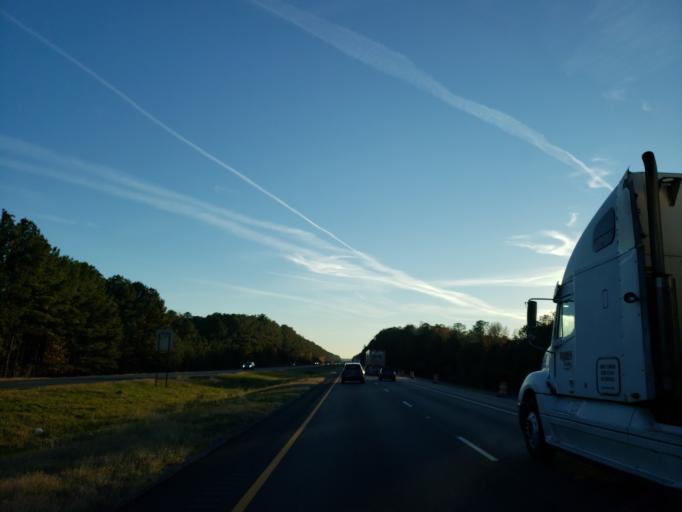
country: US
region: Alabama
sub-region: Hale County
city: Moundville
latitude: 33.0397
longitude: -87.7329
